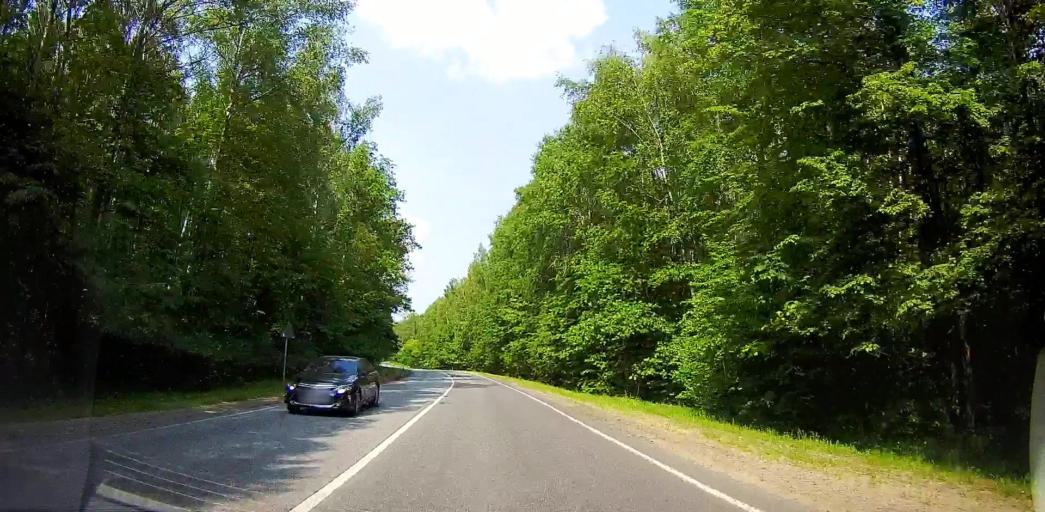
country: RU
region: Moskovskaya
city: Stupino
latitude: 54.9815
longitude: 38.1667
